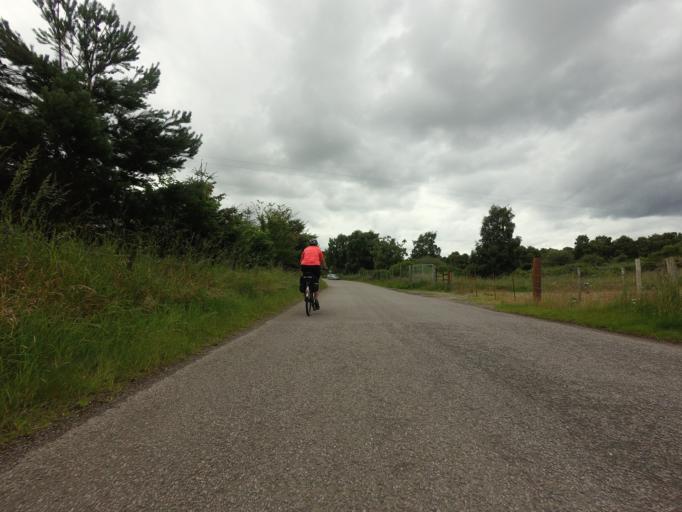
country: GB
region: Scotland
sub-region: Highland
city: Nairn
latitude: 57.5987
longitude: -3.8020
